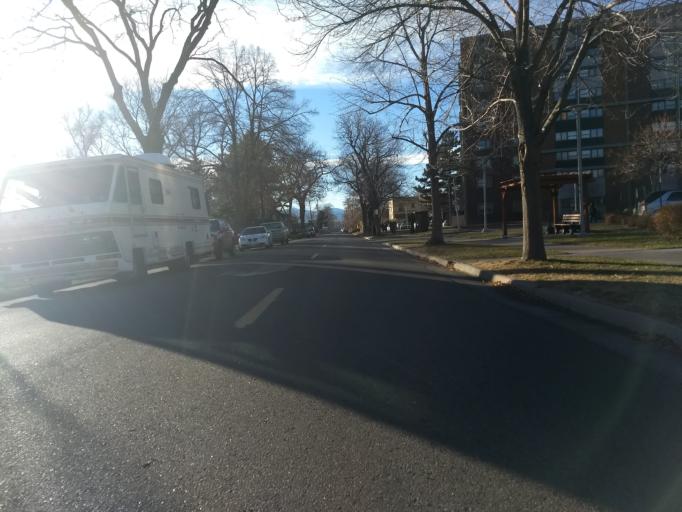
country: US
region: Colorado
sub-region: Denver County
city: Denver
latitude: 39.7166
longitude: -104.9925
